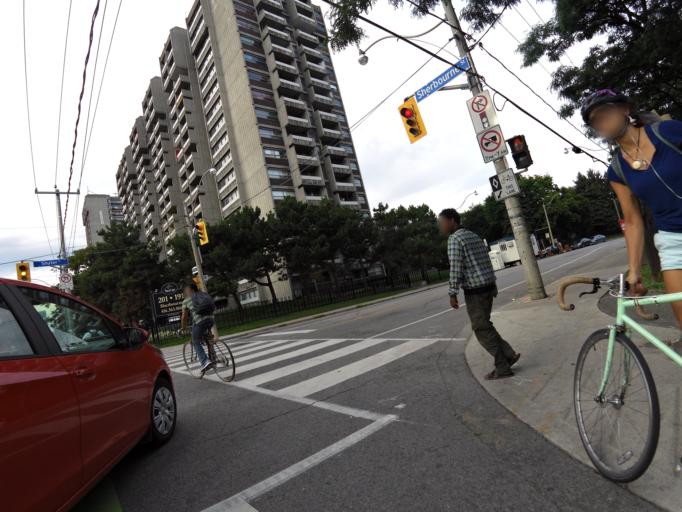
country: CA
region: Ontario
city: Toronto
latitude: 43.6561
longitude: -79.3700
